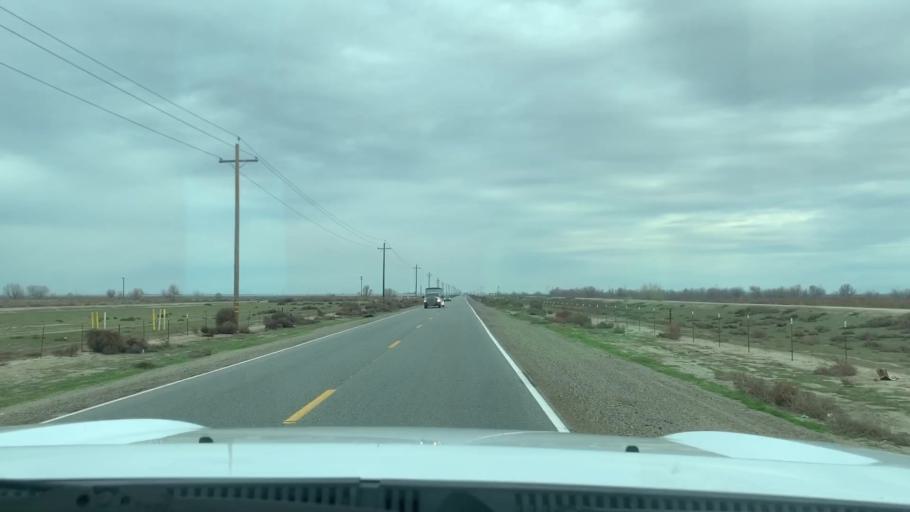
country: US
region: California
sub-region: Kern County
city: Rosedale
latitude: 35.3295
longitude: -119.2524
